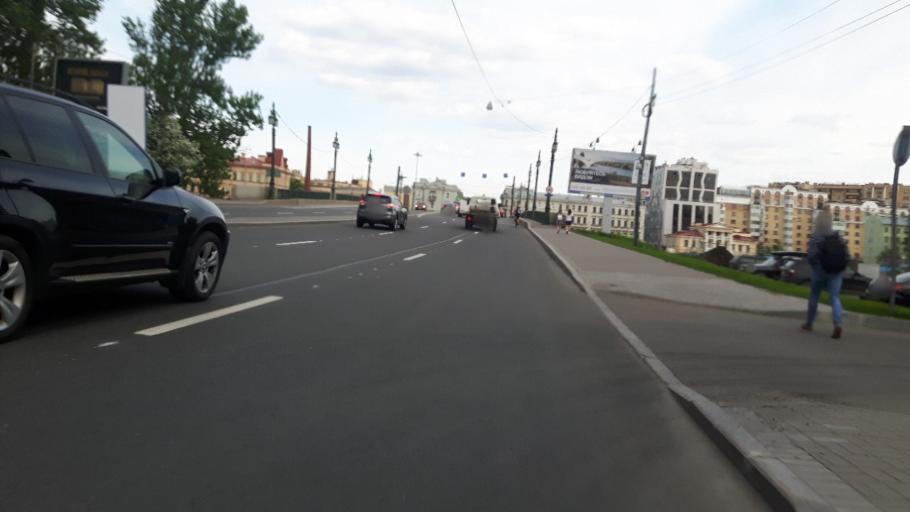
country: RU
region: Leningrad
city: Krestovskiy ostrov
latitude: 59.9679
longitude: 30.2785
